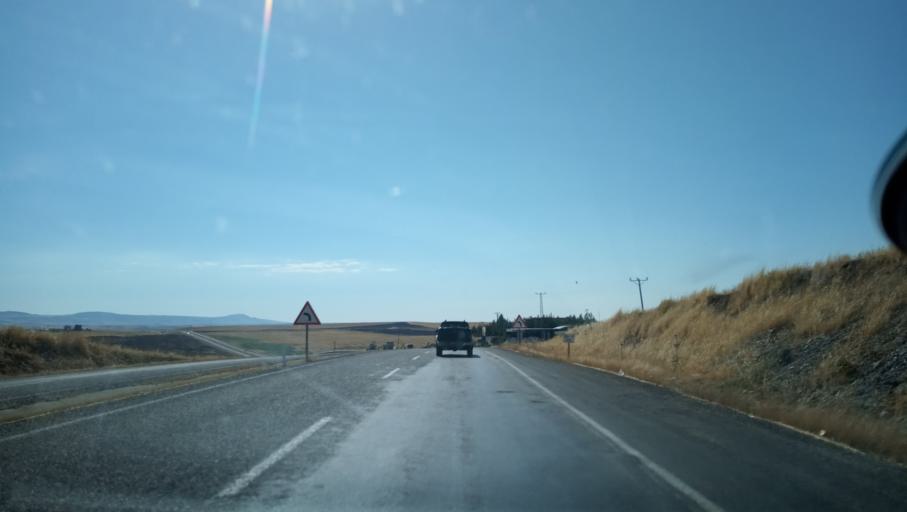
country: TR
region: Diyarbakir
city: Bagdere
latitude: 38.1287
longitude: 40.7764
